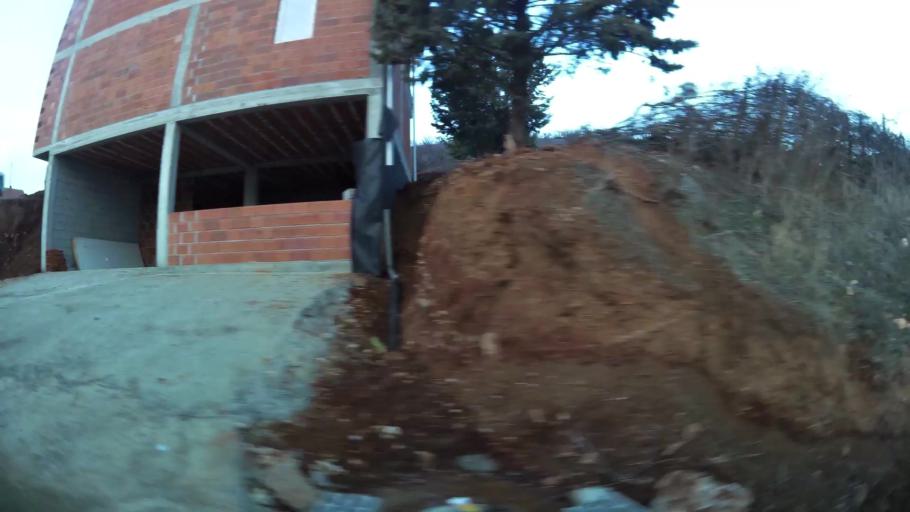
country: MK
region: Aracinovo
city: Arachinovo
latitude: 42.0319
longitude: 21.5560
